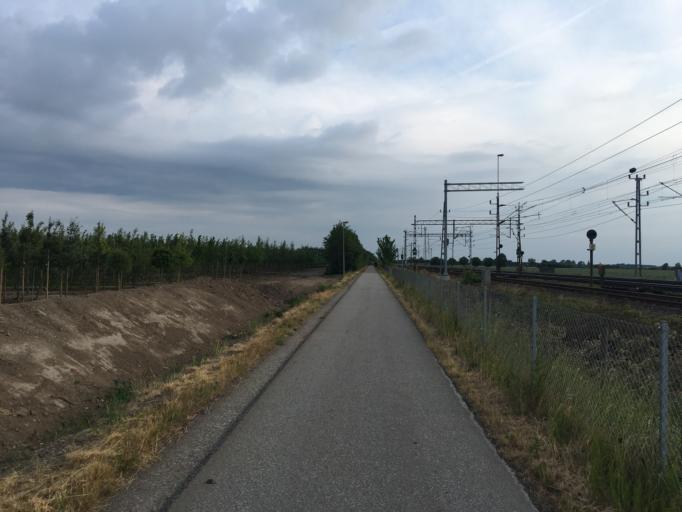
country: SE
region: Skane
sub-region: Lunds Kommun
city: Lund
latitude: 55.7431
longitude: 13.1942
